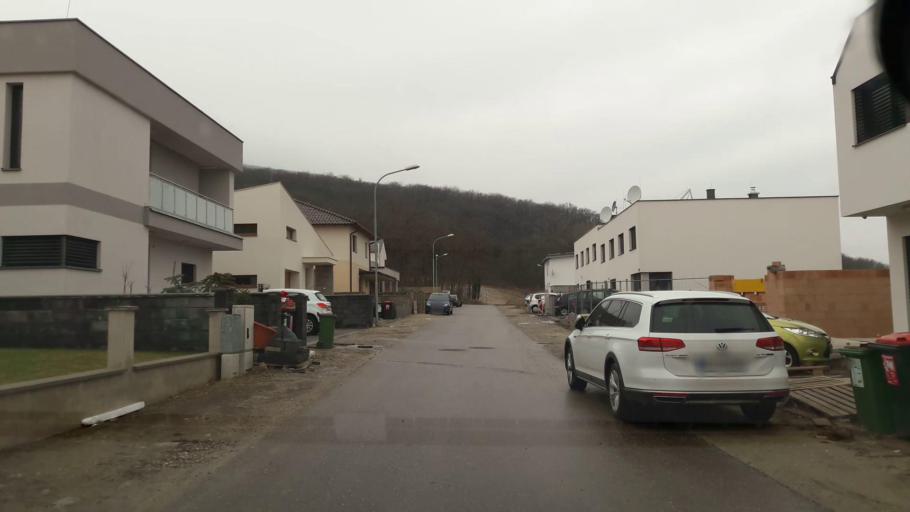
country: AT
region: Lower Austria
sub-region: Politischer Bezirk Bruck an der Leitha
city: Hainburg an der Donau
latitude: 48.1374
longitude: 16.9557
